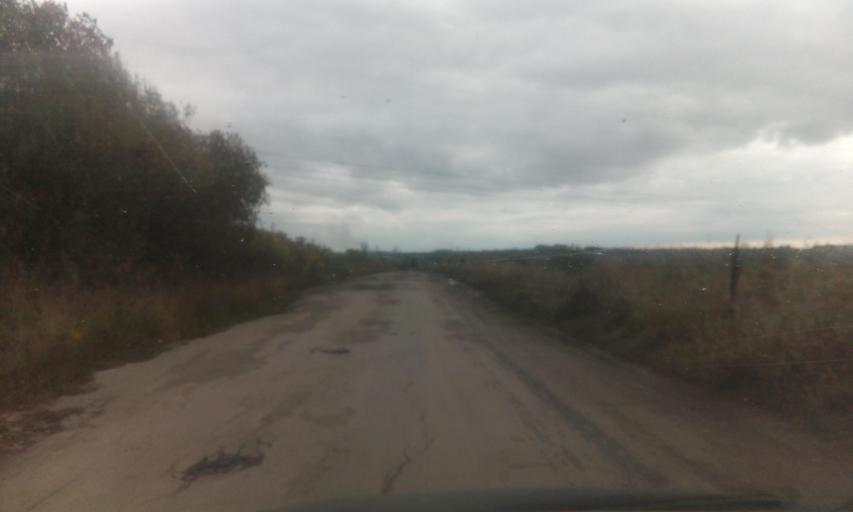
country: RU
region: Tula
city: Gritsovskiy
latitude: 54.1298
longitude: 38.1595
